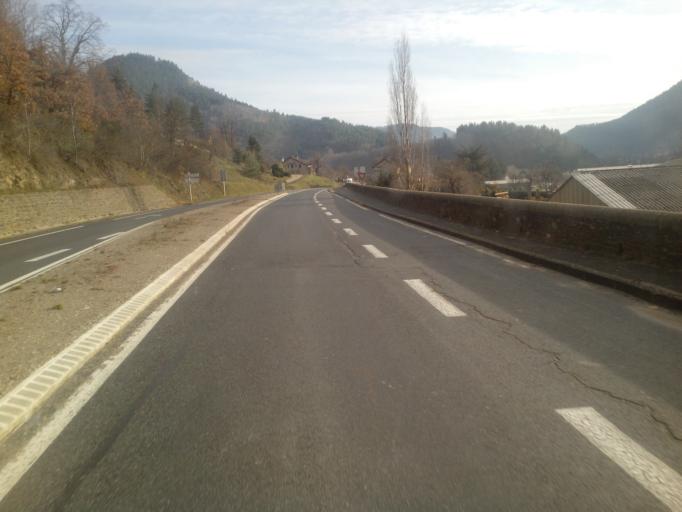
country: FR
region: Languedoc-Roussillon
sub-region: Departement de la Lozere
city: Florac
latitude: 44.3429
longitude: 3.5834
